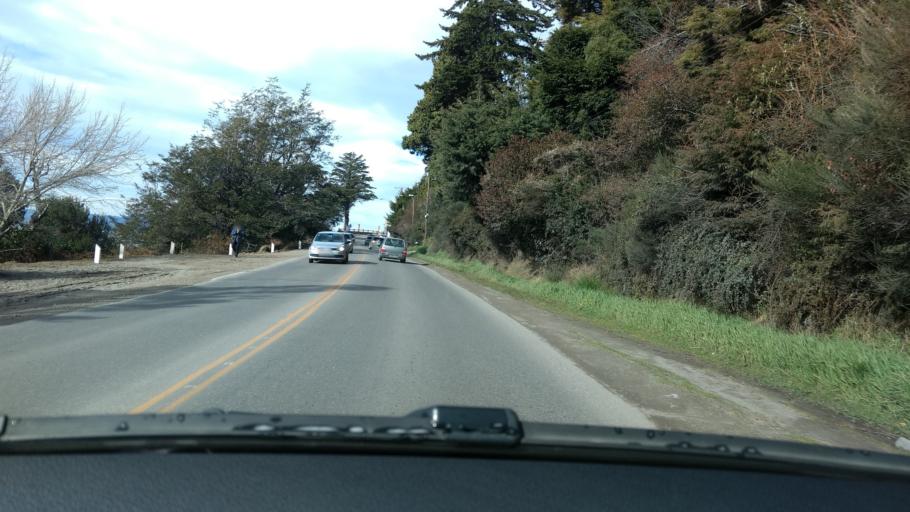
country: AR
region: Rio Negro
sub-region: Departamento de Bariloche
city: San Carlos de Bariloche
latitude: -41.1317
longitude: -71.3288
